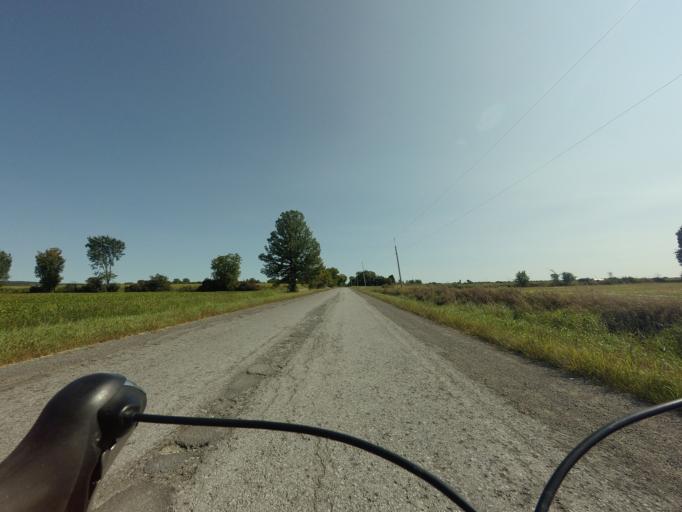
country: CA
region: Ontario
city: Carleton Place
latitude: 45.3632
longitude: -76.1288
